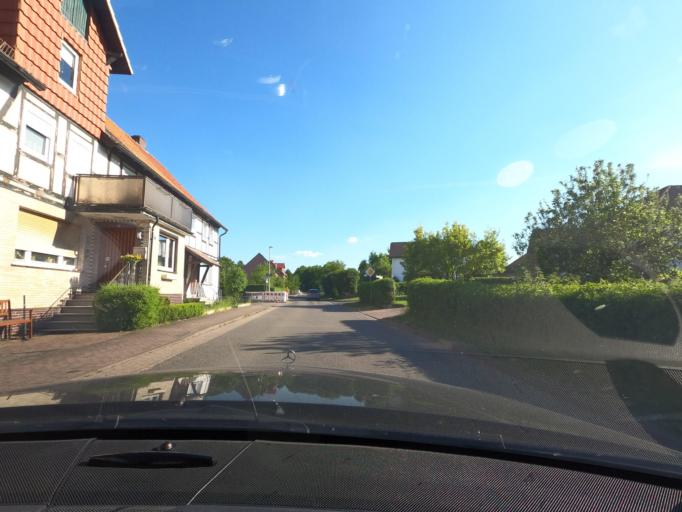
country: DE
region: Hesse
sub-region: Regierungsbezirk Kassel
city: Wolfhagen
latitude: 51.3524
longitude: 9.2087
